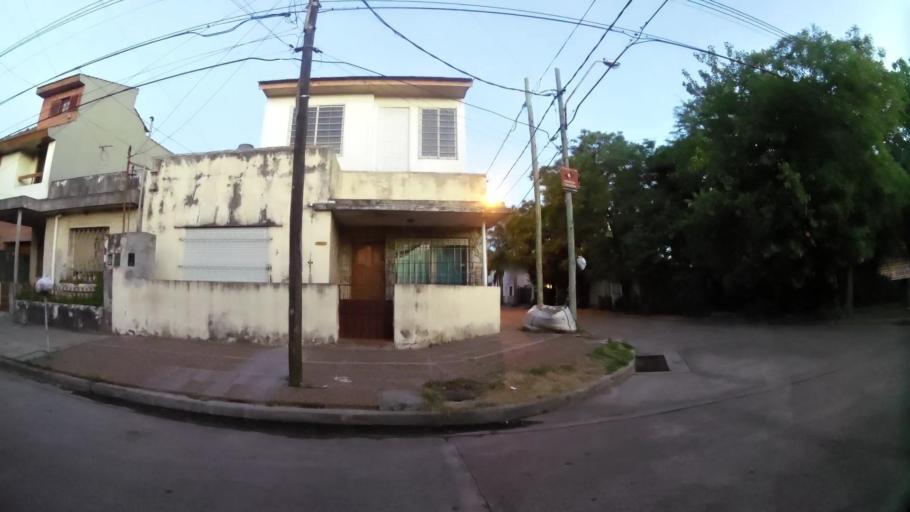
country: AR
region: Buenos Aires
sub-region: Partido de Moron
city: Moron
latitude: -34.6586
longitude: -58.6330
